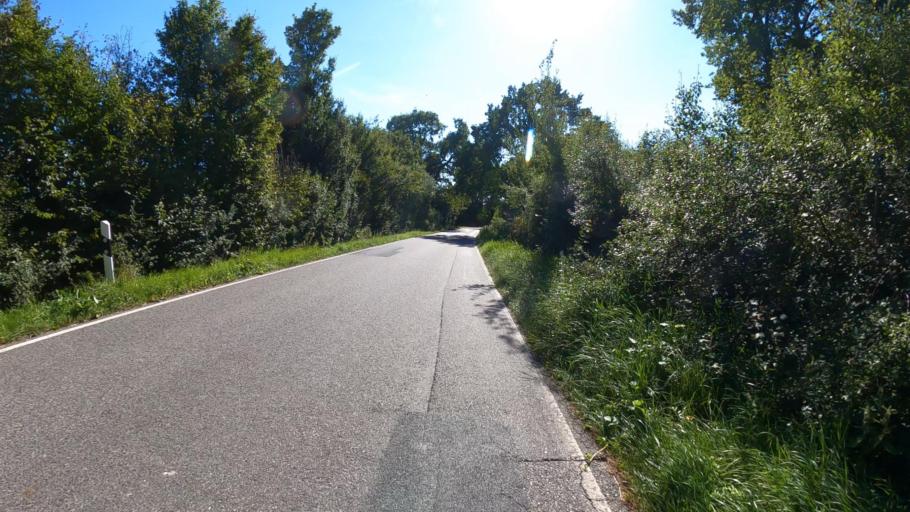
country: DE
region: Schleswig-Holstein
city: Westerau
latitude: 53.7738
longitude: 10.5197
